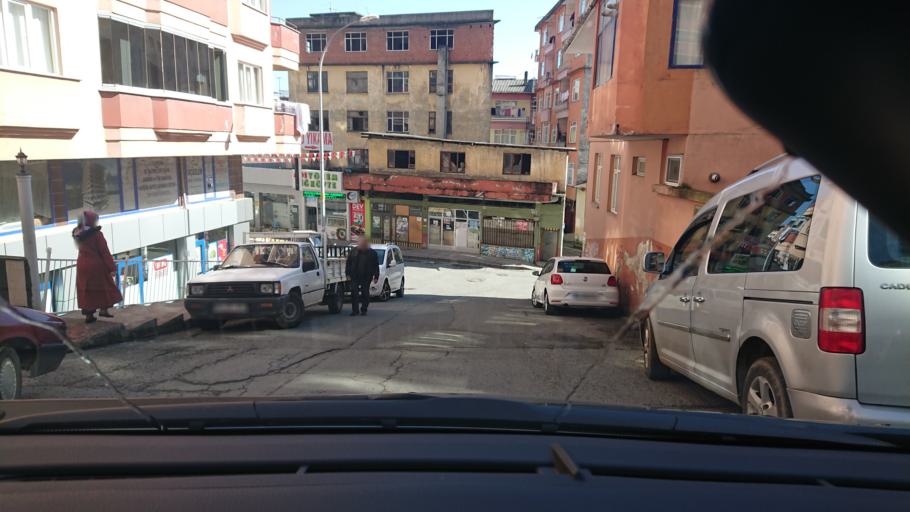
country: TR
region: Rize
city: Rize
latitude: 41.0227
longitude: 40.5258
